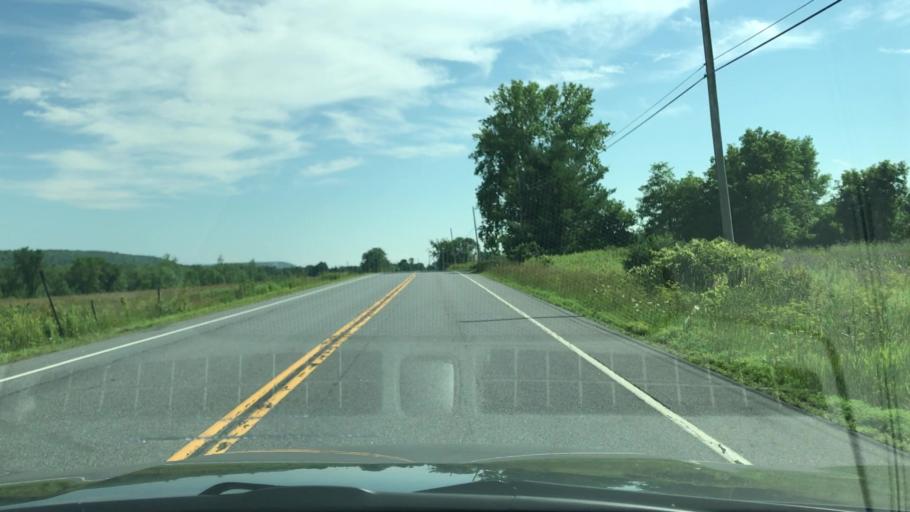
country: US
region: New York
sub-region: Washington County
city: Whitehall
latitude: 43.5169
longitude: -73.4150
